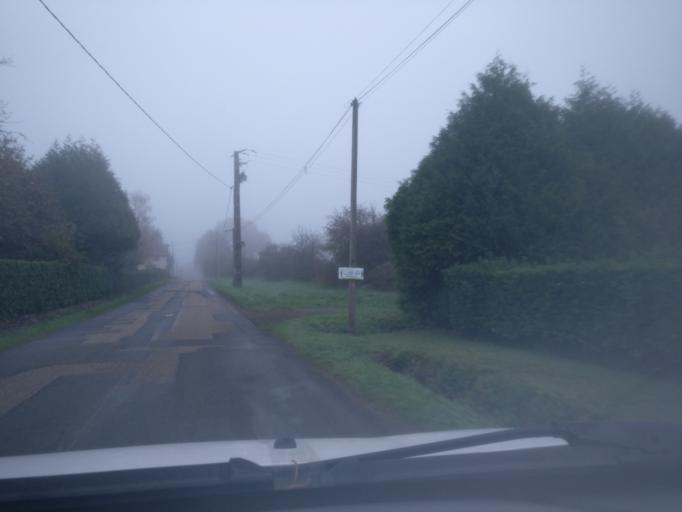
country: FR
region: Brittany
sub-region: Departement d'Ille-et-Vilaine
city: Laille
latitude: 47.9930
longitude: -1.7144
